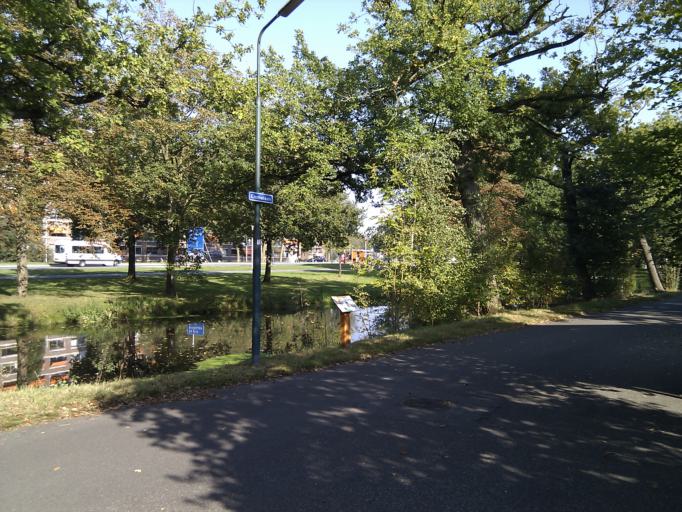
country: NL
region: Utrecht
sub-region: Gemeente De Bilt
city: De Bilt
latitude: 52.1026
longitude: 5.1809
